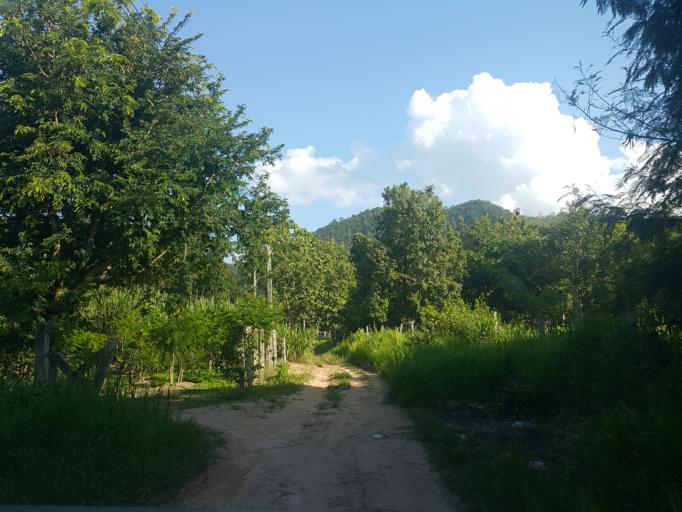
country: TH
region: Chiang Mai
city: Mae On
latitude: 18.7142
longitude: 99.2109
